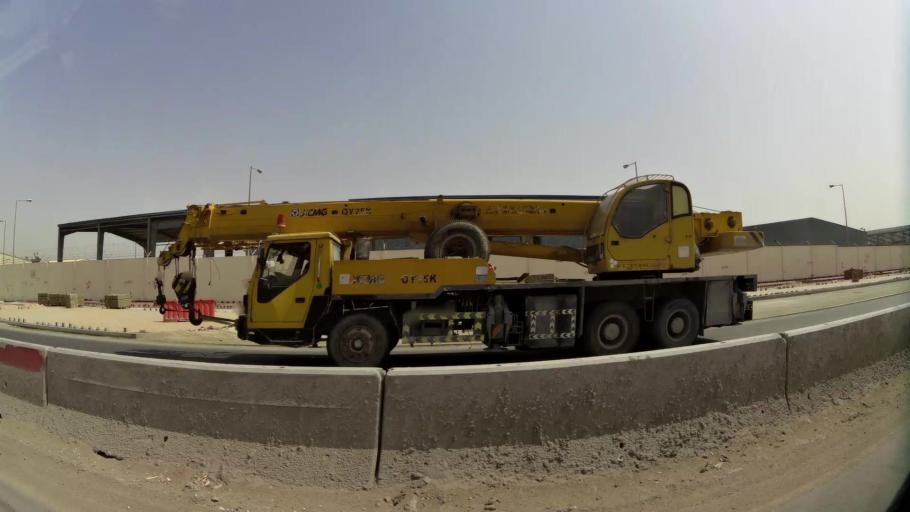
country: QA
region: Baladiyat ar Rayyan
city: Ar Rayyan
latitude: 25.2033
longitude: 51.4116
